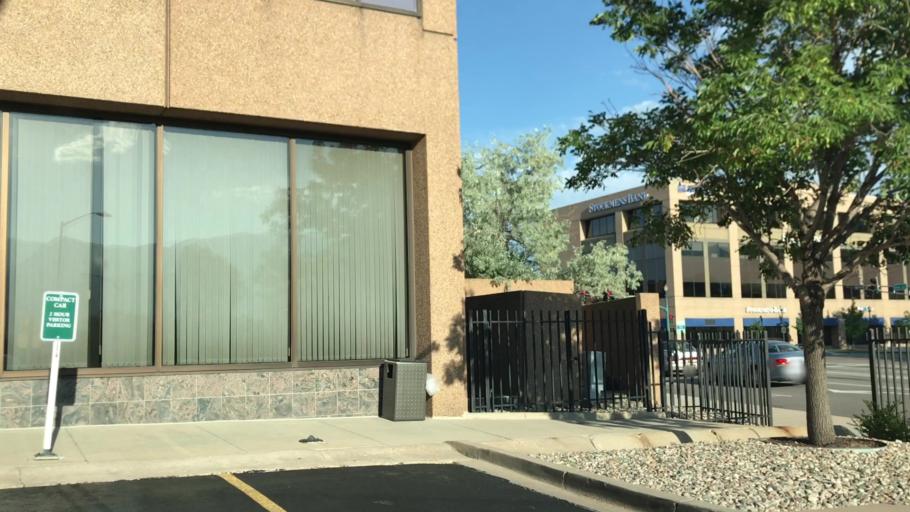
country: US
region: Colorado
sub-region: El Paso County
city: Colorado Springs
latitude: 38.8359
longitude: -104.8259
